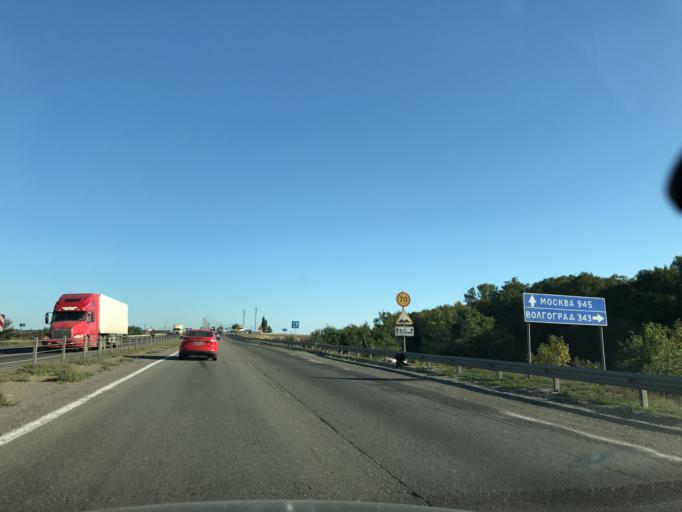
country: RU
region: Rostov
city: Likhoy
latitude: 48.1833
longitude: 40.2654
